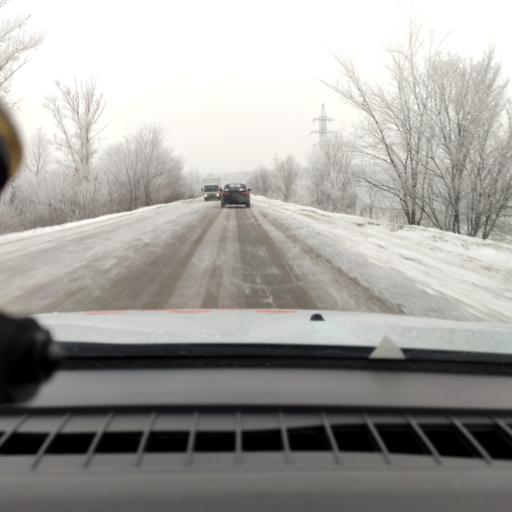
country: RU
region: Samara
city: Samara
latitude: 53.1107
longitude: 50.2252
